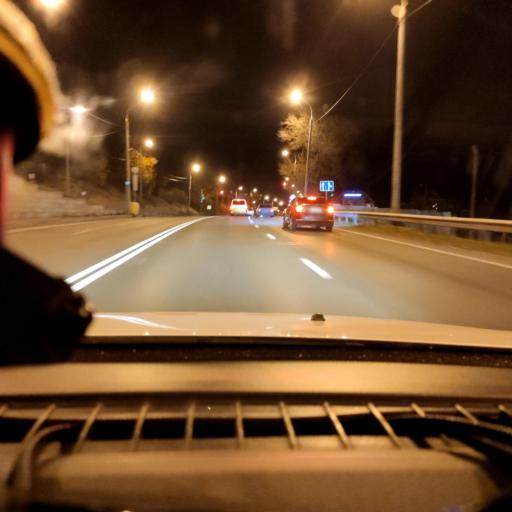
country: RU
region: Samara
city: Volzhskiy
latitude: 53.4322
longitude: 50.1170
